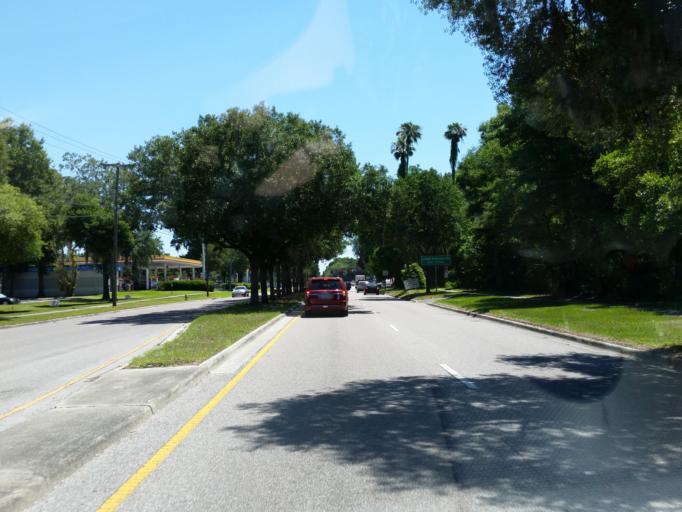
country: US
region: Florida
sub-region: Hillsborough County
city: Brandon
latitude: 27.9231
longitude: -82.2728
